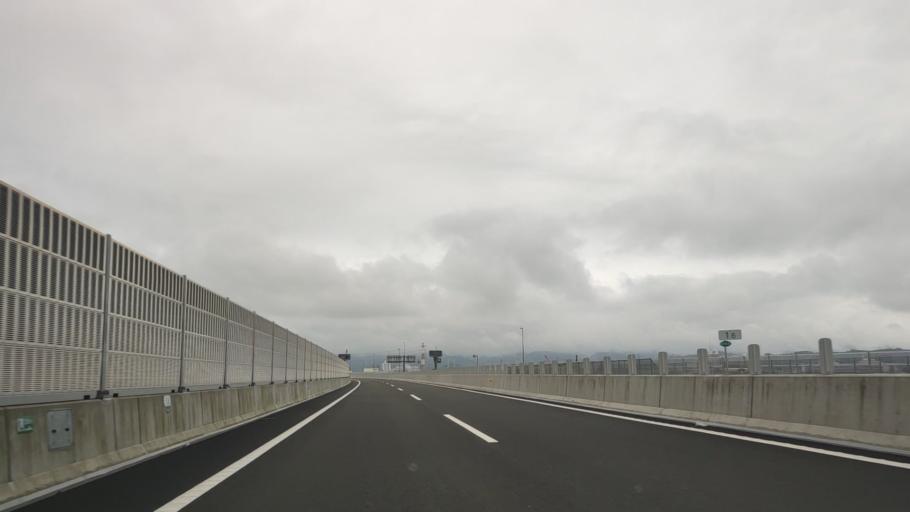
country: JP
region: Kanagawa
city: Atsugi
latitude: 35.4063
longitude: 139.3545
